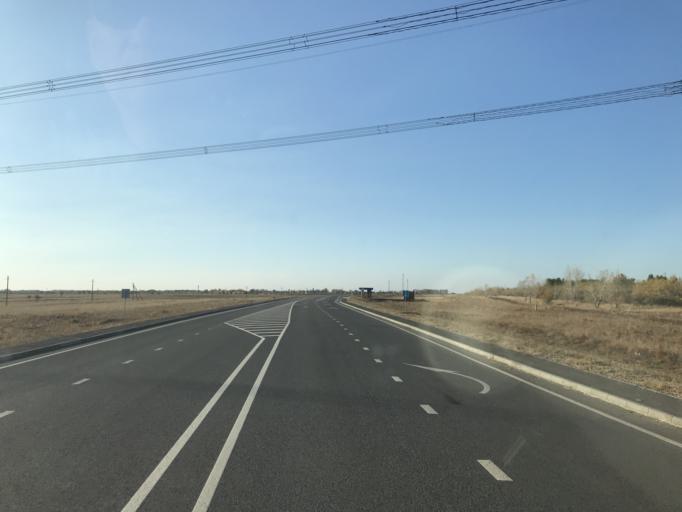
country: KZ
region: Pavlodar
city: Koktobe
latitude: 51.9096
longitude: 77.3576
